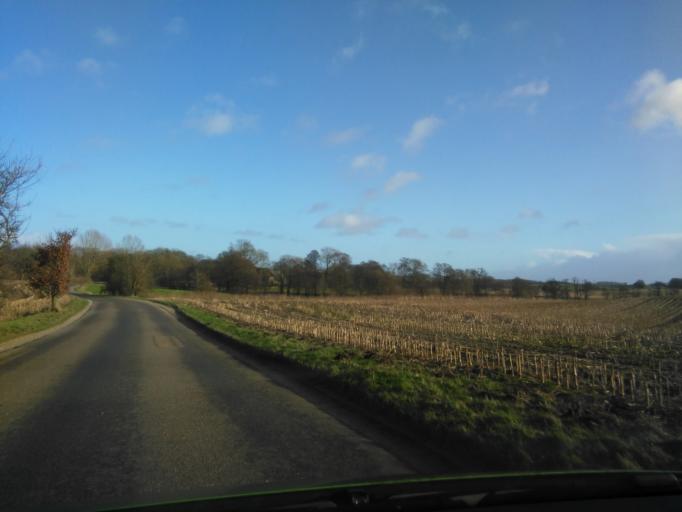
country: DK
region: Central Jutland
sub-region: Skanderborg Kommune
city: Skanderborg
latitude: 56.0127
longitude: 9.9595
